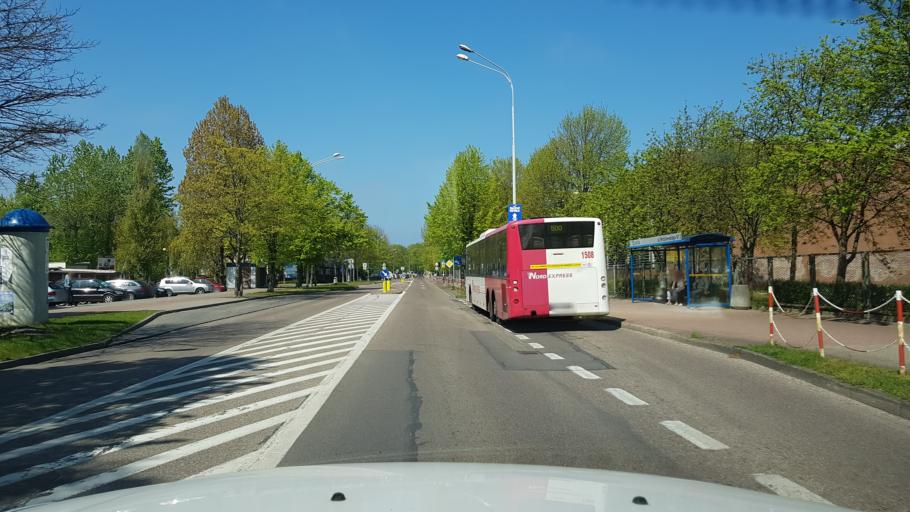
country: PL
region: Pomeranian Voivodeship
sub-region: Powiat slupski
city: Ustka
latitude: 54.5780
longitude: 16.8675
